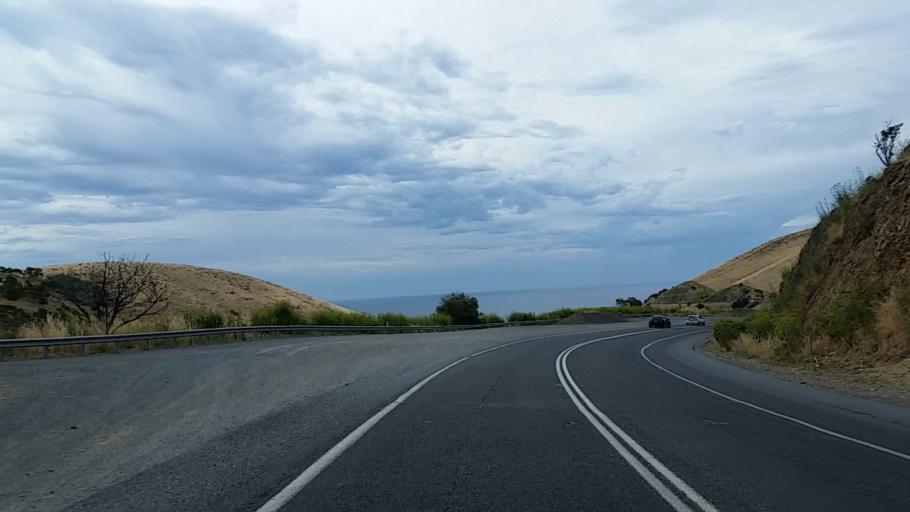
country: AU
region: South Australia
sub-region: Onkaparinga
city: Aldinga
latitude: -35.3630
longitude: 138.4542
